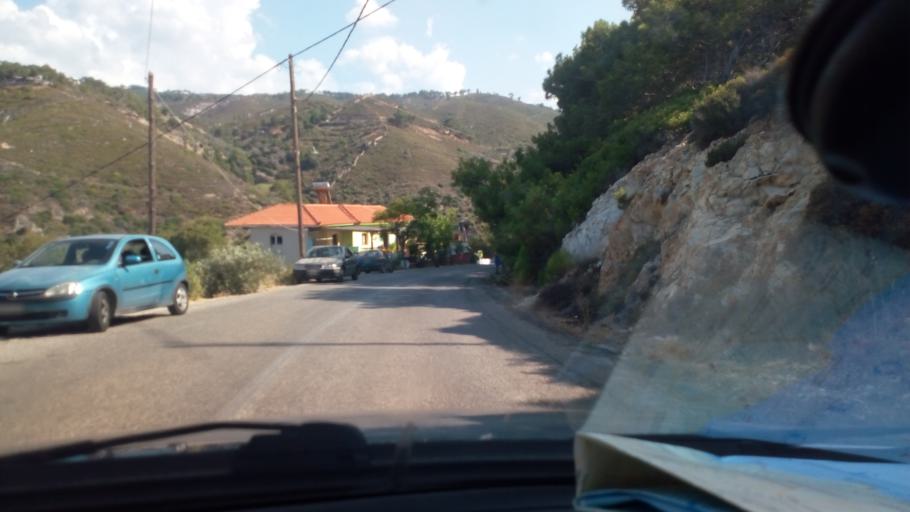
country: GR
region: North Aegean
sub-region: Nomos Samou
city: Agios Kirykos
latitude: 37.6302
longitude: 26.0890
